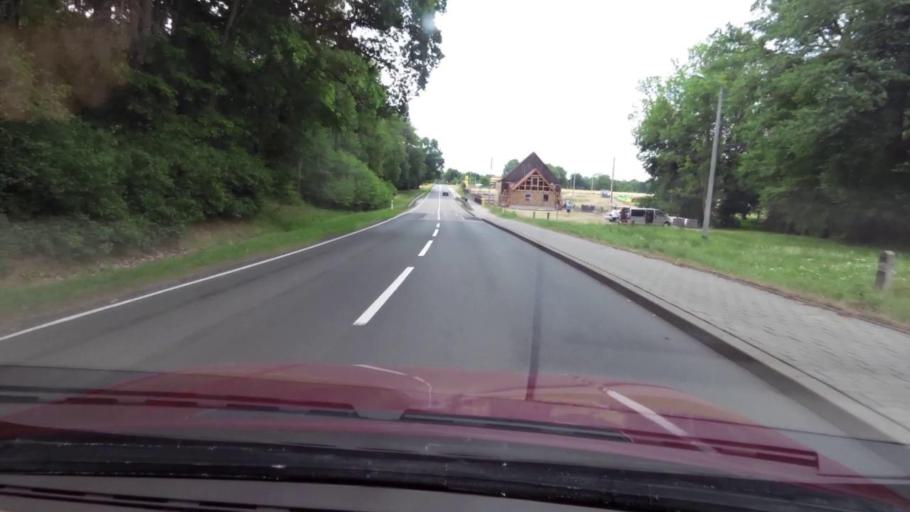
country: PL
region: Pomeranian Voivodeship
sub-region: Powiat bytowski
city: Trzebielino
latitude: 54.2077
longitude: 17.0899
